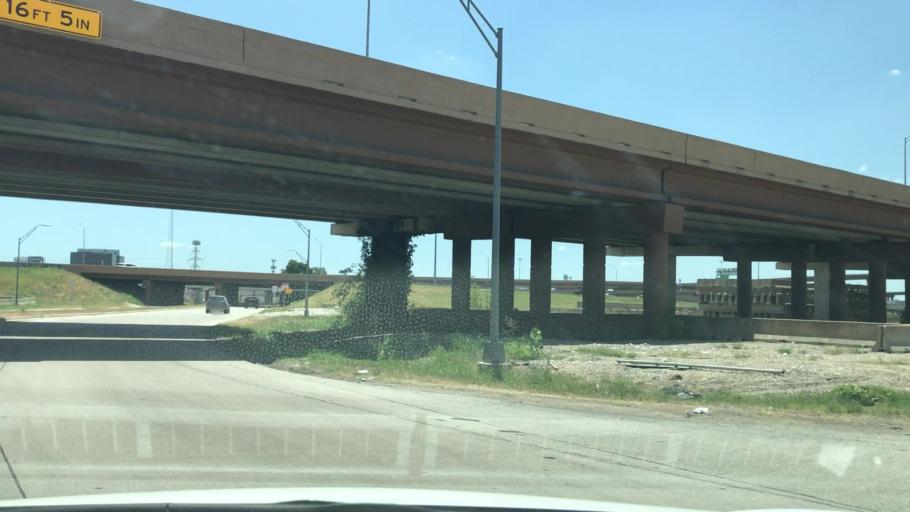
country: US
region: Texas
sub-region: Dallas County
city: Farmers Branch
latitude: 32.9142
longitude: -96.8998
